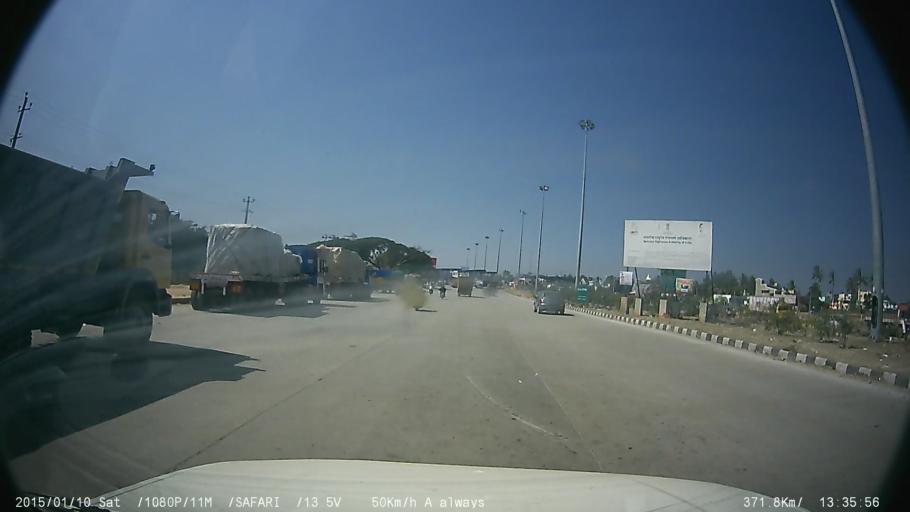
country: IN
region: Tamil Nadu
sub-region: Krishnagiri
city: Hosur
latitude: 12.7753
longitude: 77.7792
